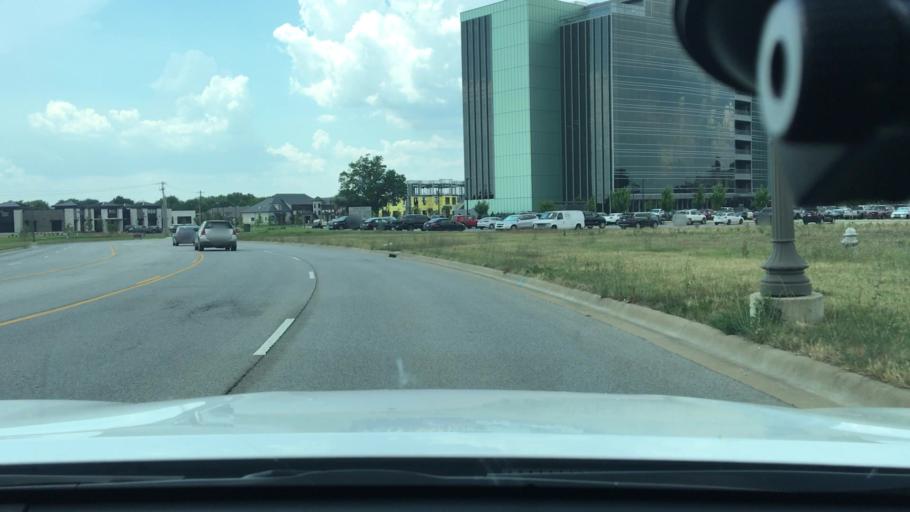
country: US
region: Arkansas
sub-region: Benton County
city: Cave Springs
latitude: 36.3003
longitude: -94.1873
